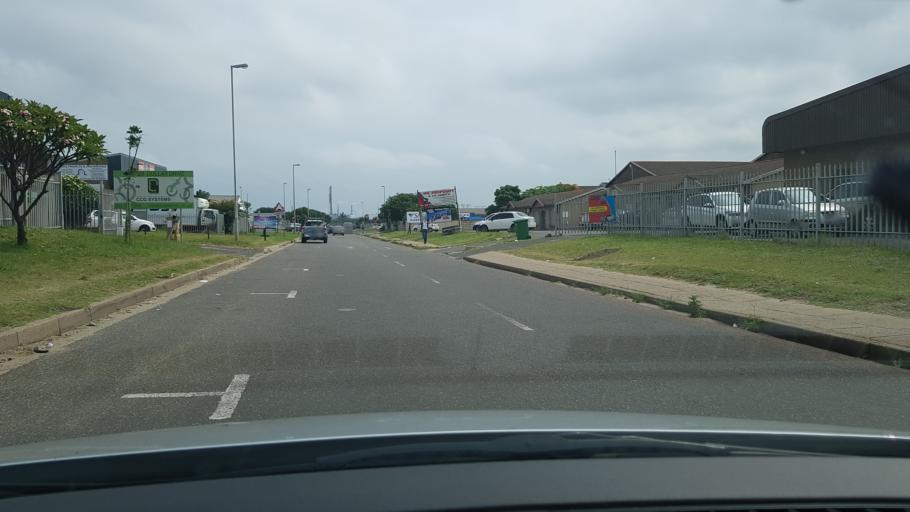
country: ZA
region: KwaZulu-Natal
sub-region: uThungulu District Municipality
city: Richards Bay
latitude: -28.7551
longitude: 32.0438
